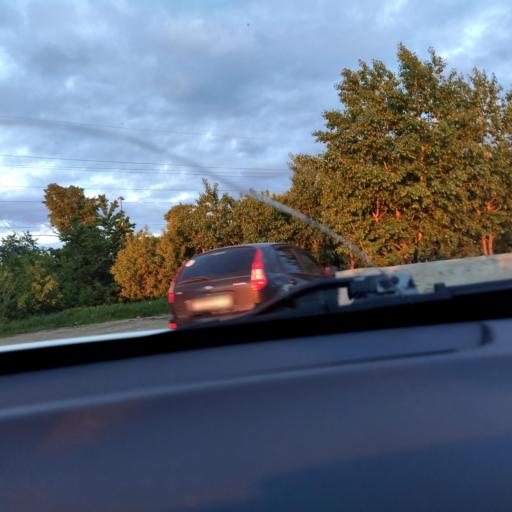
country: RU
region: Tatarstan
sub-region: Gorod Kazan'
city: Kazan
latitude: 55.7877
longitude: 49.0967
